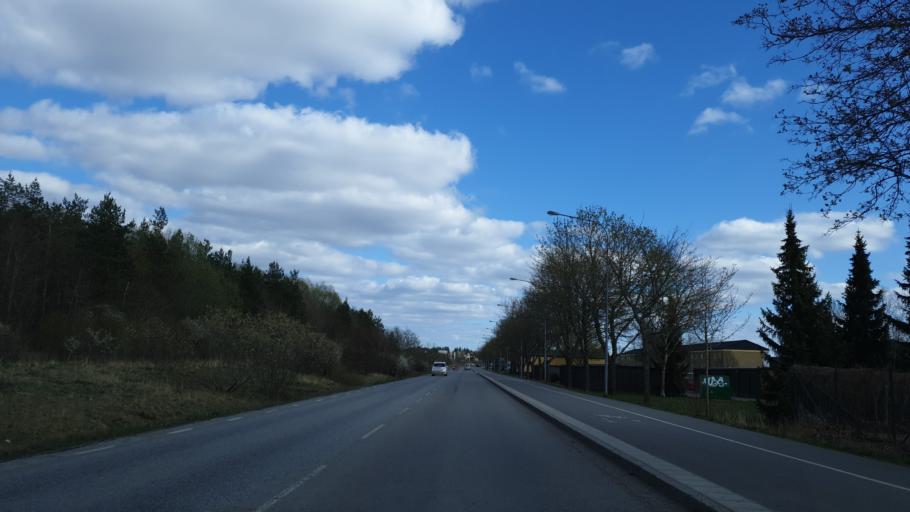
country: SE
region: Uppsala
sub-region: Uppsala Kommun
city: Gamla Uppsala
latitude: 59.8897
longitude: 17.6552
